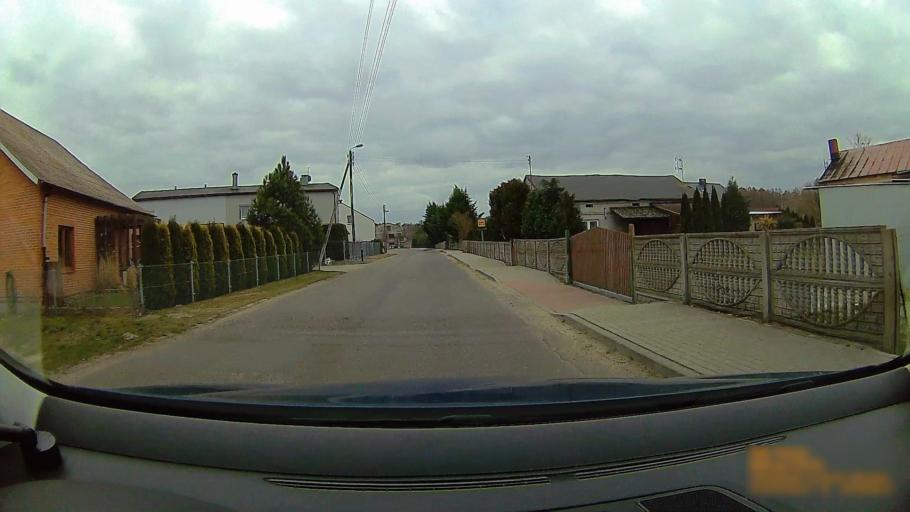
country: PL
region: Greater Poland Voivodeship
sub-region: Powiat koninski
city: Rzgow Pierwszy
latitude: 52.1322
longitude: 18.0584
